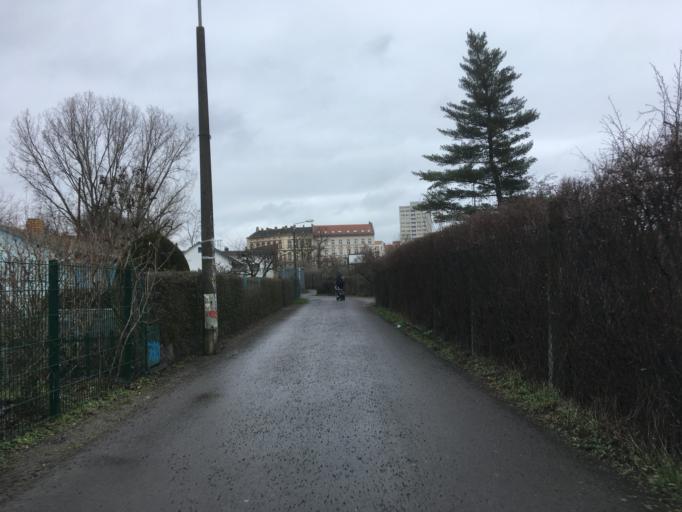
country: DE
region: Berlin
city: Friedrichsfelde
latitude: 52.5039
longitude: 13.5142
